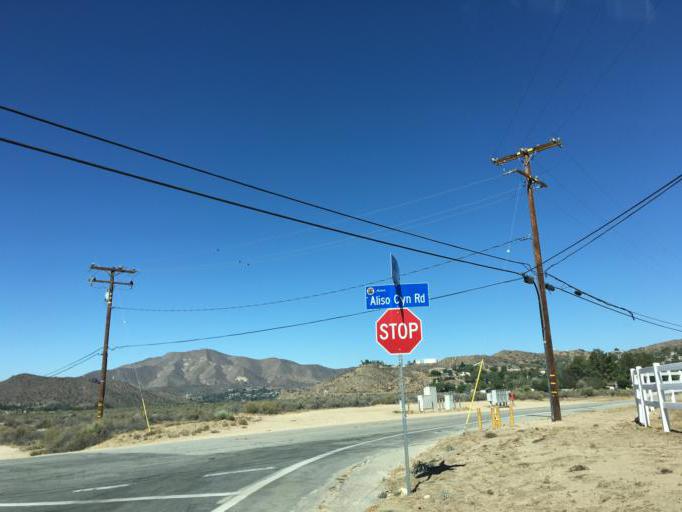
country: US
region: California
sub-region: Los Angeles County
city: Acton
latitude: 34.4730
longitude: -118.1636
